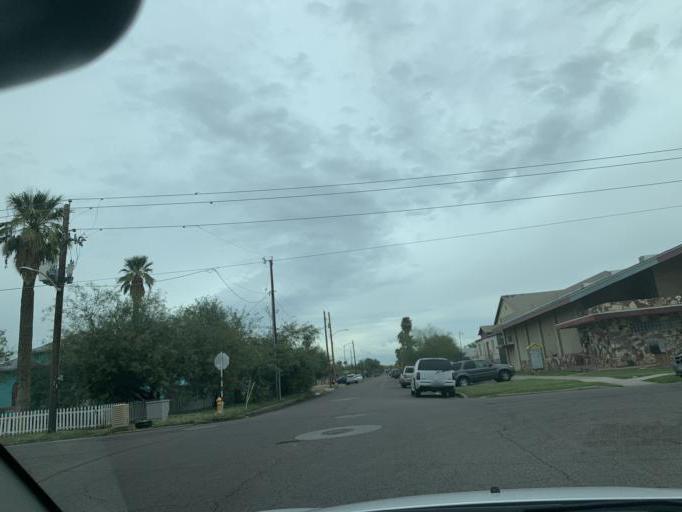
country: US
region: Arizona
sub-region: Maricopa County
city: Phoenix
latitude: 33.4600
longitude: -112.0609
